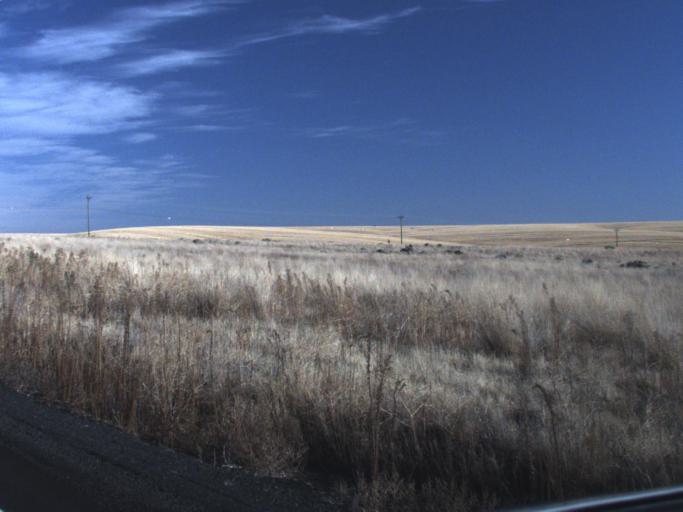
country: US
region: Washington
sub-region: Adams County
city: Ritzville
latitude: 47.1287
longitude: -118.6651
